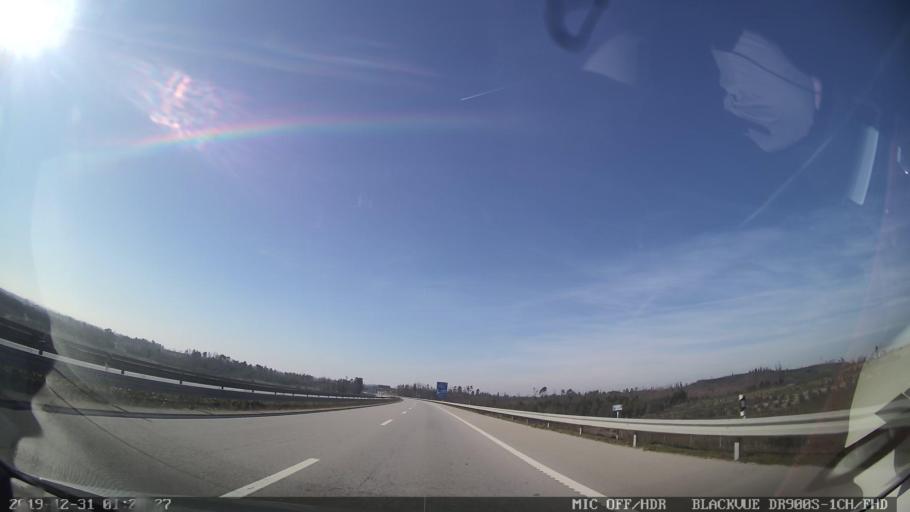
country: PT
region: Santarem
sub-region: Macao
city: Macao
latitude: 39.5354
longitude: -7.9321
